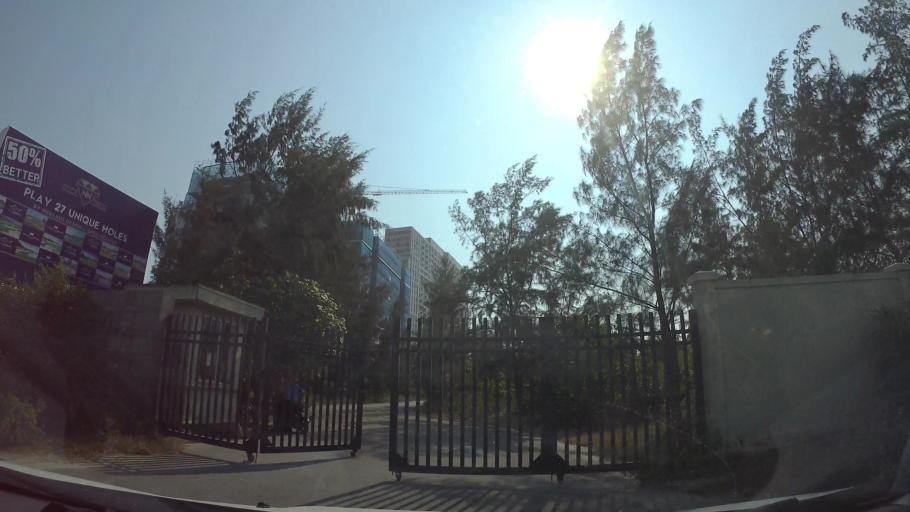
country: VN
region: Da Nang
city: Ngu Hanh Son
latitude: 15.9684
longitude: 108.2838
